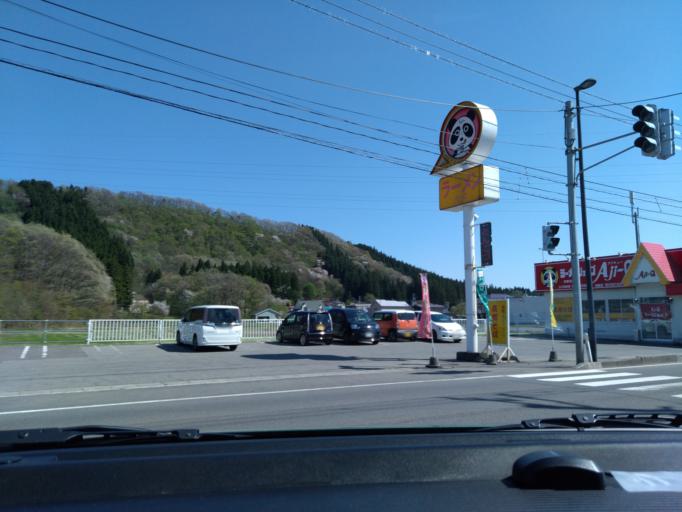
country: JP
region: Akita
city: Kakunodatemachi
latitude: 39.5904
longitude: 140.5739
